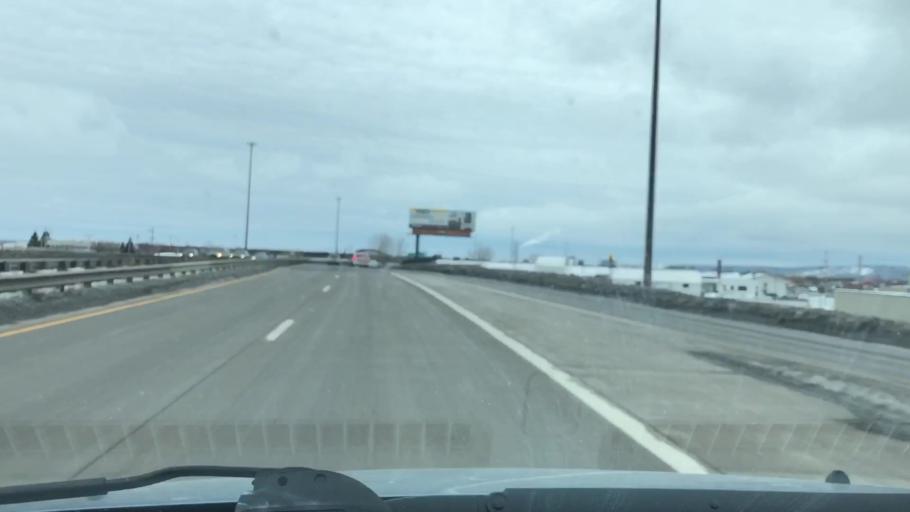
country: US
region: Minnesota
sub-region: Saint Louis County
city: Duluth
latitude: 46.7631
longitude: -92.1255
